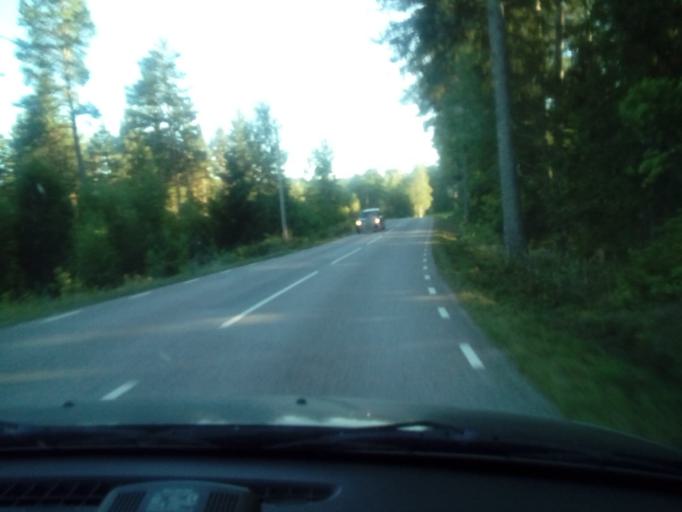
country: SE
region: Kalmar
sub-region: Vasterviks Kommun
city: Gamleby
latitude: 57.7991
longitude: 16.4154
